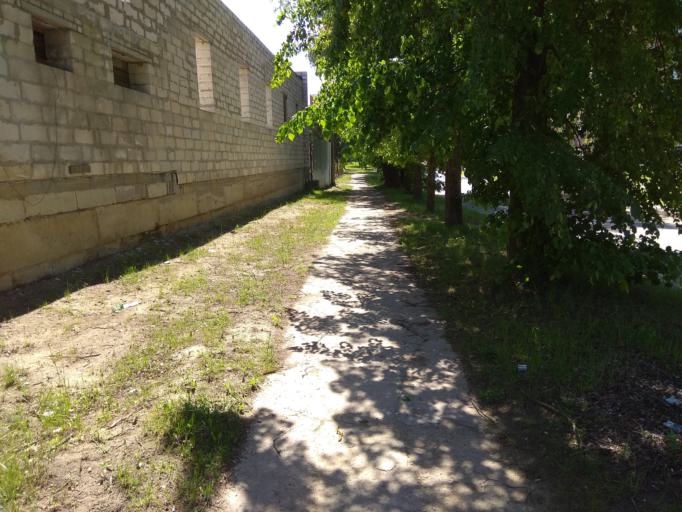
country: BY
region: Grodnenskaya
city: Hrodna
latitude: 53.7106
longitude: 23.8026
